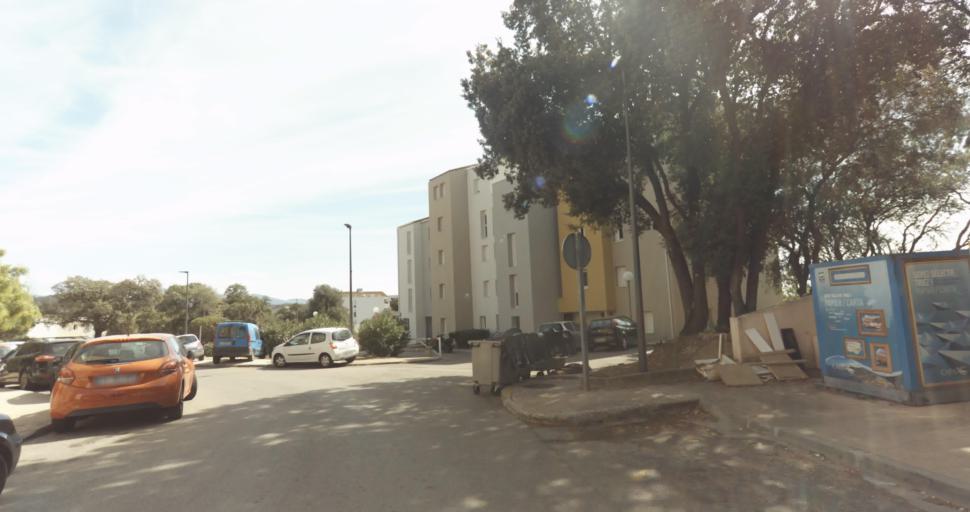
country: FR
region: Corsica
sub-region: Departement de la Corse-du-Sud
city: Ajaccio
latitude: 41.9479
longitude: 8.7534
